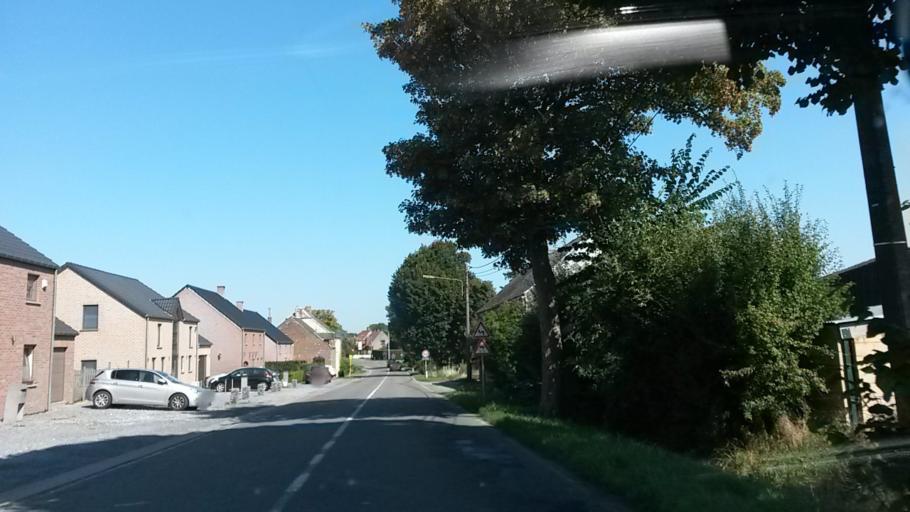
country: BE
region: Wallonia
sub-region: Province du Hainaut
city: Merbes-le-Chateau
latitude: 50.3511
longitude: 4.1776
